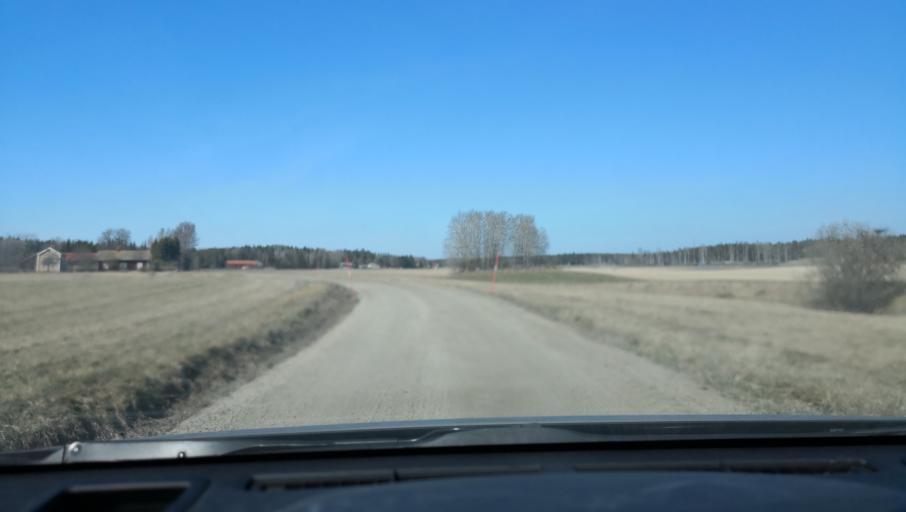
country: SE
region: Vaestmanland
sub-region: Sala Kommun
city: Sala
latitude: 59.8972
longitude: 16.5298
